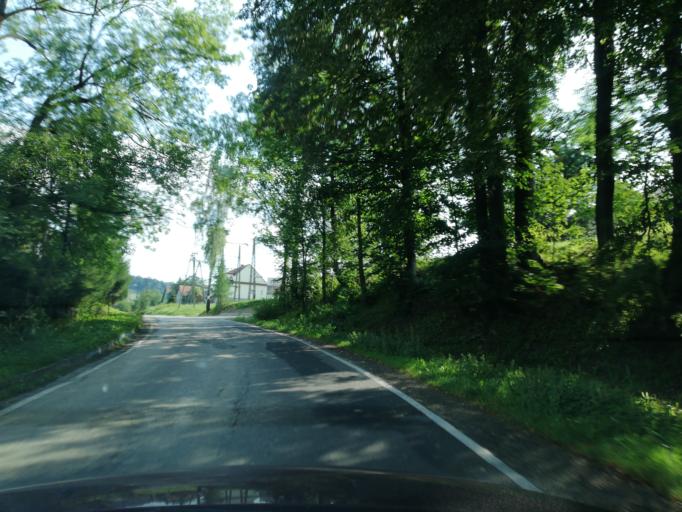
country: PL
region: Lesser Poland Voivodeship
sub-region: Powiat nowosadecki
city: Nawojowa
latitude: 49.5522
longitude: 20.7447
